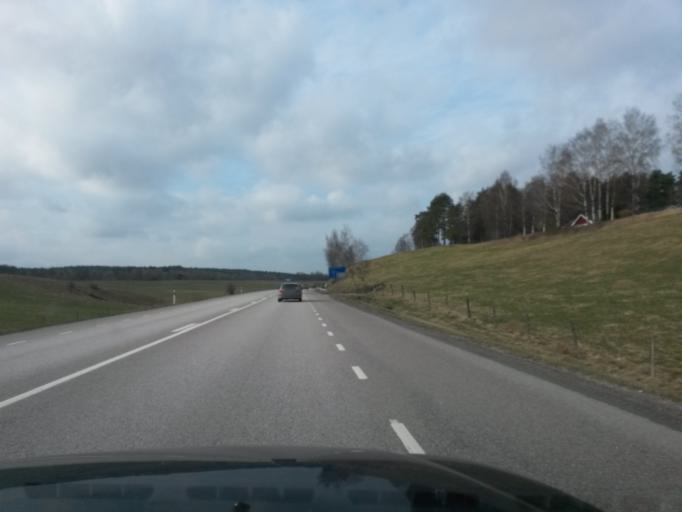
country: SE
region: Vaestra Goetaland
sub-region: Vargarda Kommun
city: Jonstorp
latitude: 57.9745
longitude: 12.6725
